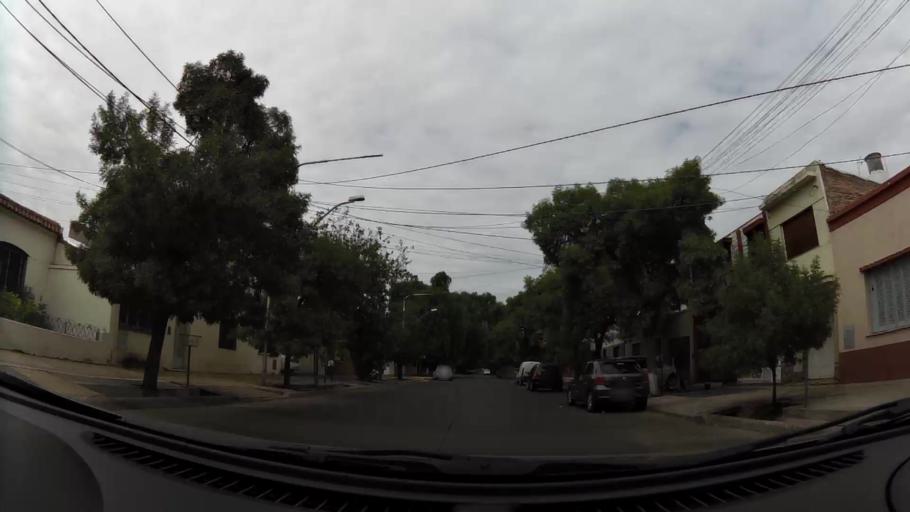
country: AR
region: Mendoza
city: Mendoza
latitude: -32.8979
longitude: -68.8569
